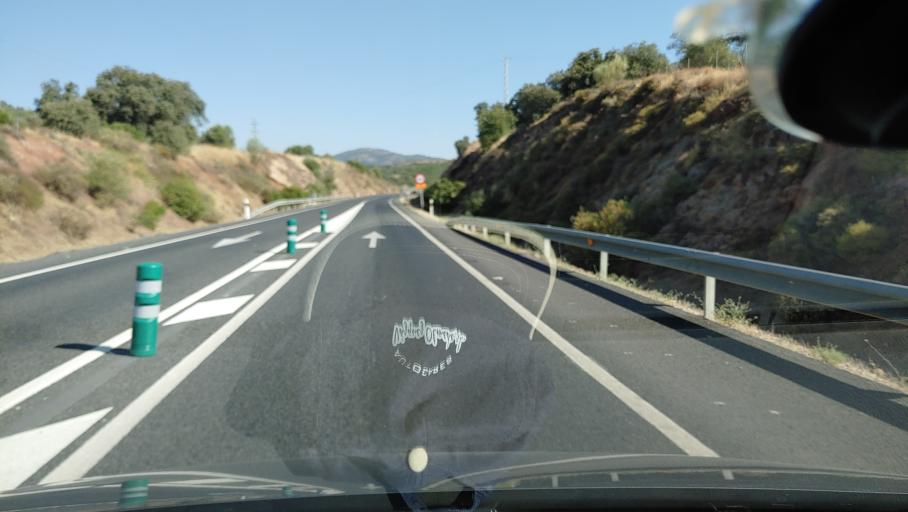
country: ES
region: Andalusia
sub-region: Province of Cordoba
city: Cordoba
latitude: 37.9257
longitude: -4.7661
